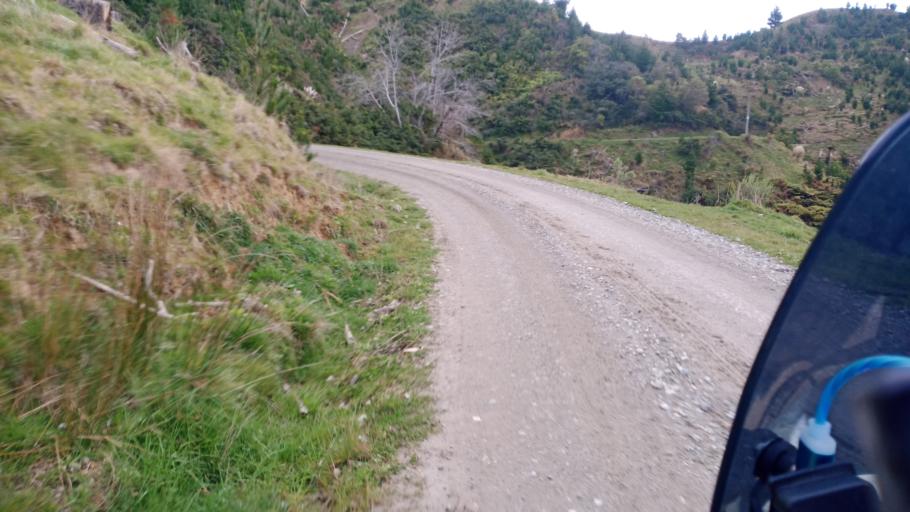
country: NZ
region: Gisborne
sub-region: Gisborne District
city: Gisborne
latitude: -38.5507
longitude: 178.1397
